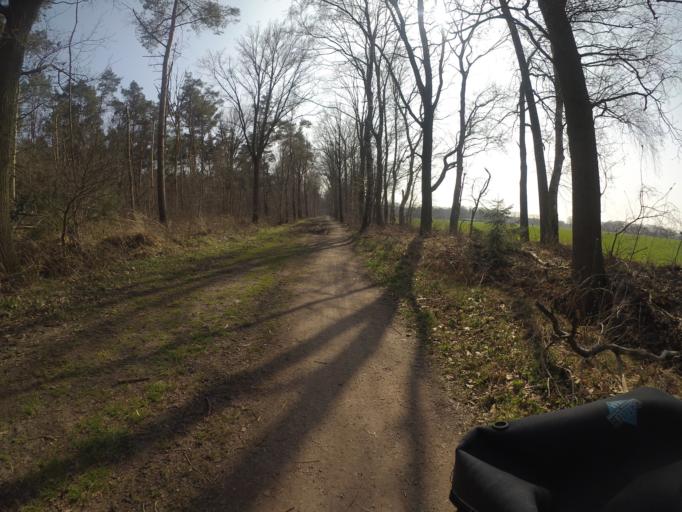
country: NL
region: North Brabant
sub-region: Gemeente Schijndel
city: Schijndel
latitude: 51.6737
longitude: 5.4508
